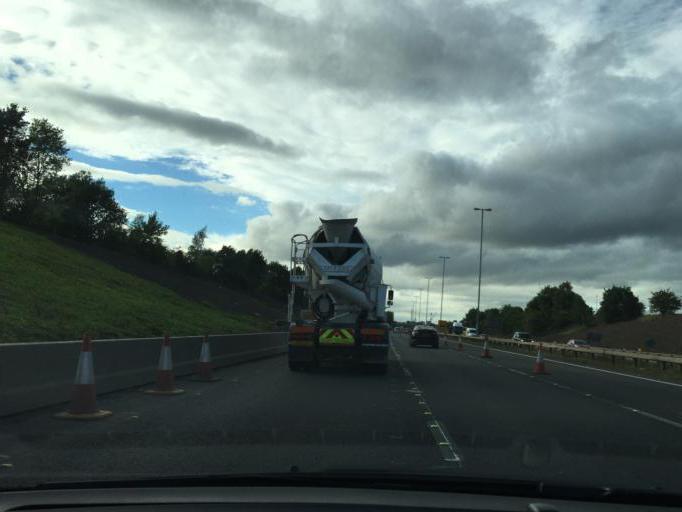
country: GB
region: Scotland
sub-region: South Lanarkshire
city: Bothwell
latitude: 55.8092
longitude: -4.0600
